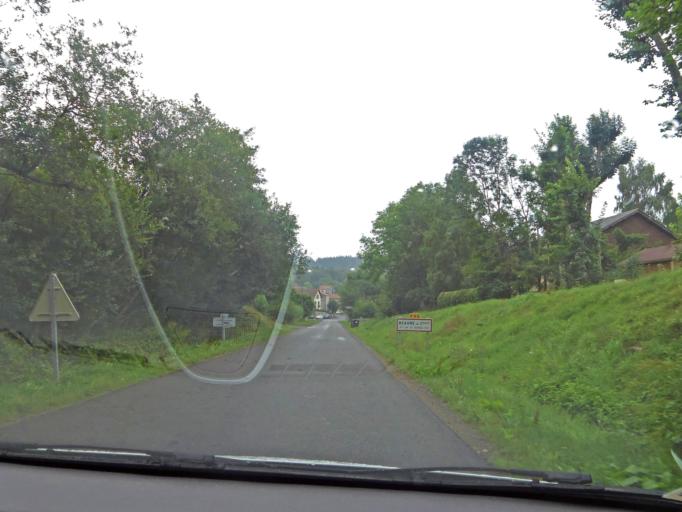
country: FR
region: Auvergne
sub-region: Departement du Puy-de-Dome
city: Saint-Genes-Champanelle
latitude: 45.7284
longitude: 2.9870
